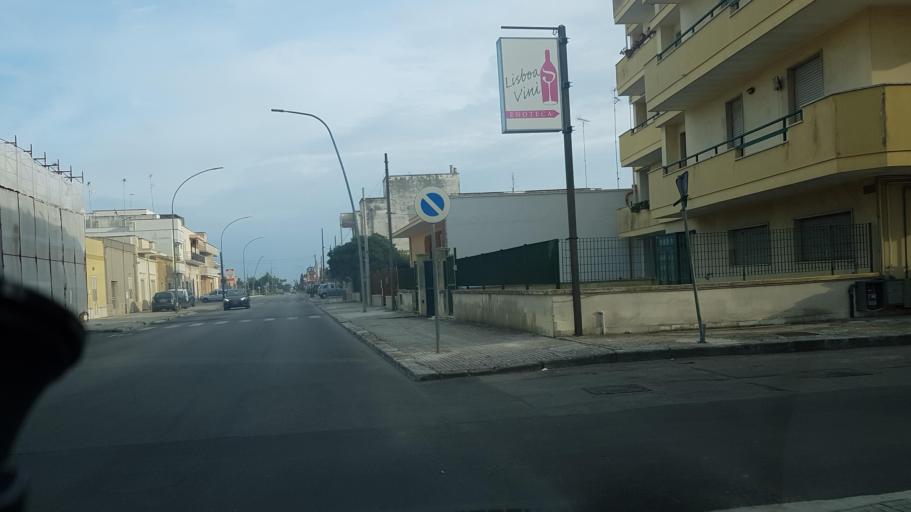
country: IT
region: Apulia
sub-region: Provincia di Lecce
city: Trepuzzi
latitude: 40.3999
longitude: 18.0813
